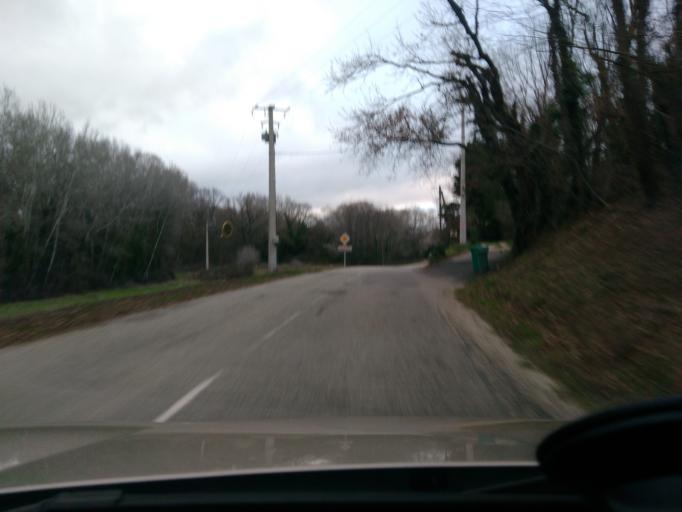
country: FR
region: Rhone-Alpes
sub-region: Departement de la Drome
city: Montelimar
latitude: 44.5615
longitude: 4.7763
